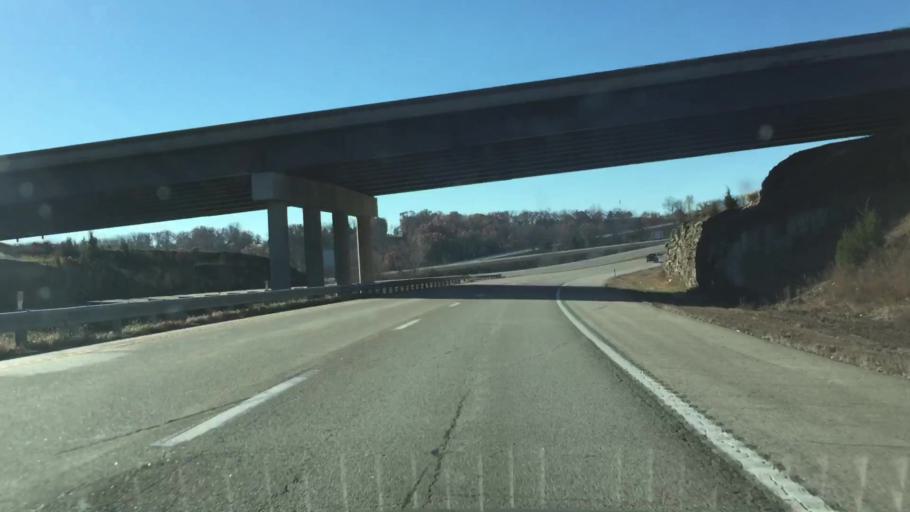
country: US
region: Missouri
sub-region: Cole County
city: Jefferson City
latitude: 38.5406
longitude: -92.2090
